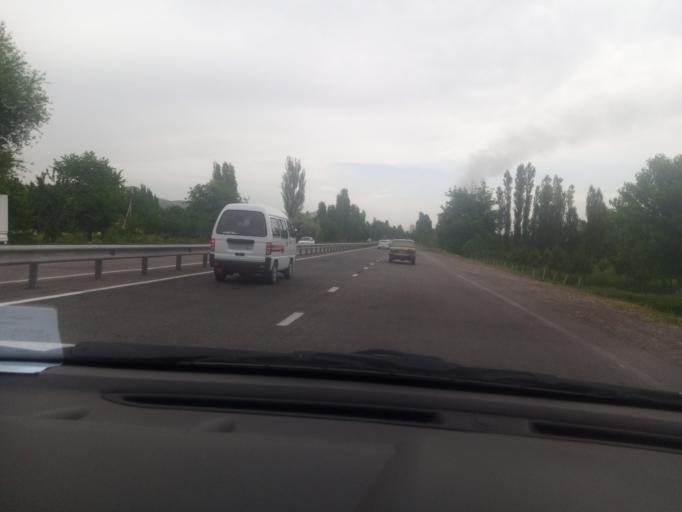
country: UZ
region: Toshkent
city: Ohangaron
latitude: 40.9080
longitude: 69.7429
